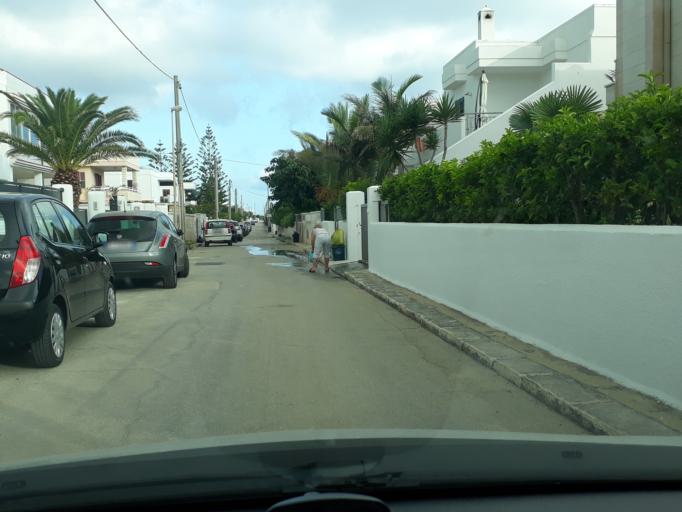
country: IT
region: Apulia
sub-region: Provincia di Brindisi
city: Carovigno
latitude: 40.7603
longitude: 17.6945
